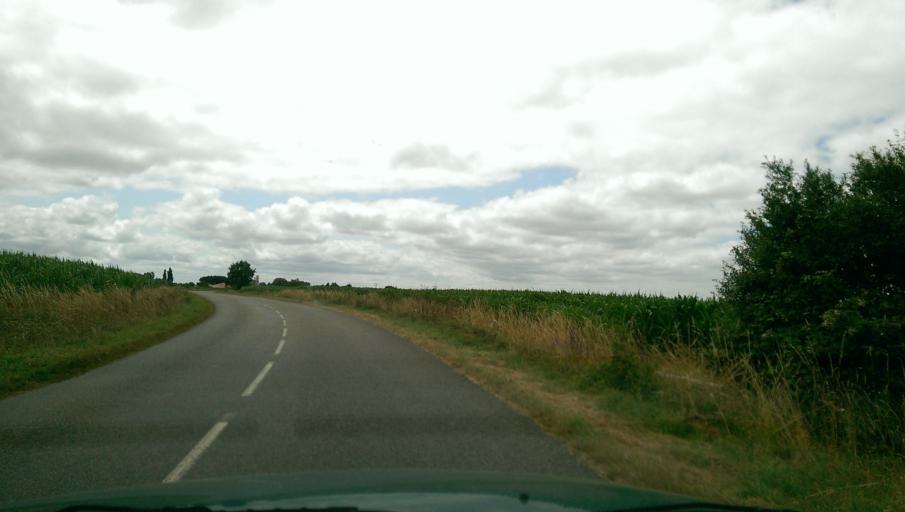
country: FR
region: Pays de la Loire
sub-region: Departement de la Loire-Atlantique
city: Vieillevigne
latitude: 46.9882
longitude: -1.4295
